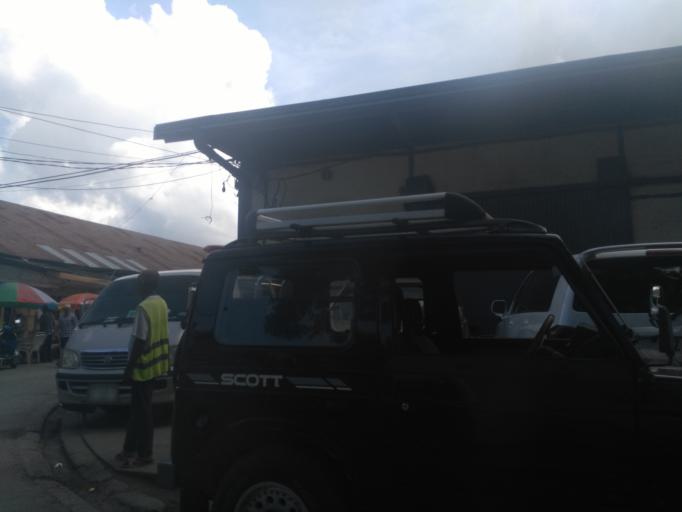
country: TZ
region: Zanzibar Urban/West
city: Zanzibar
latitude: -6.1563
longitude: 39.1934
